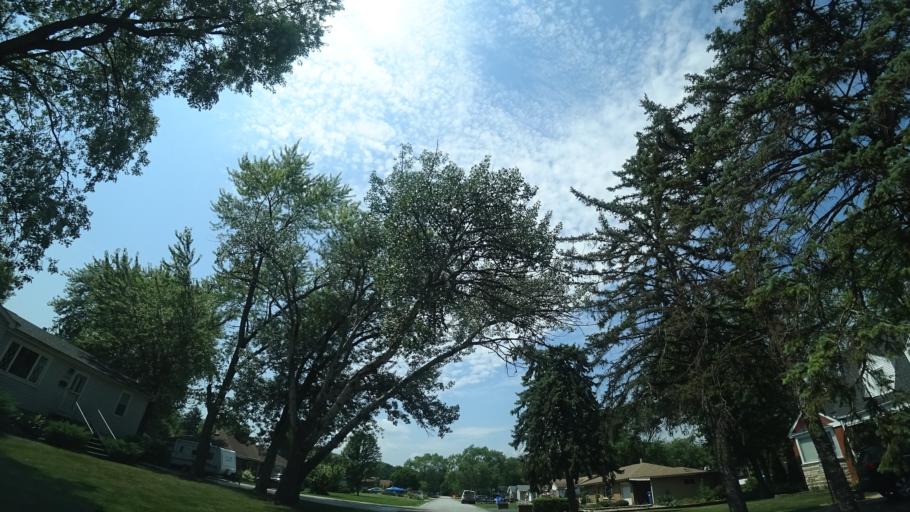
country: US
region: Illinois
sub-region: Cook County
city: Worth
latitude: 41.6874
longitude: -87.7895
